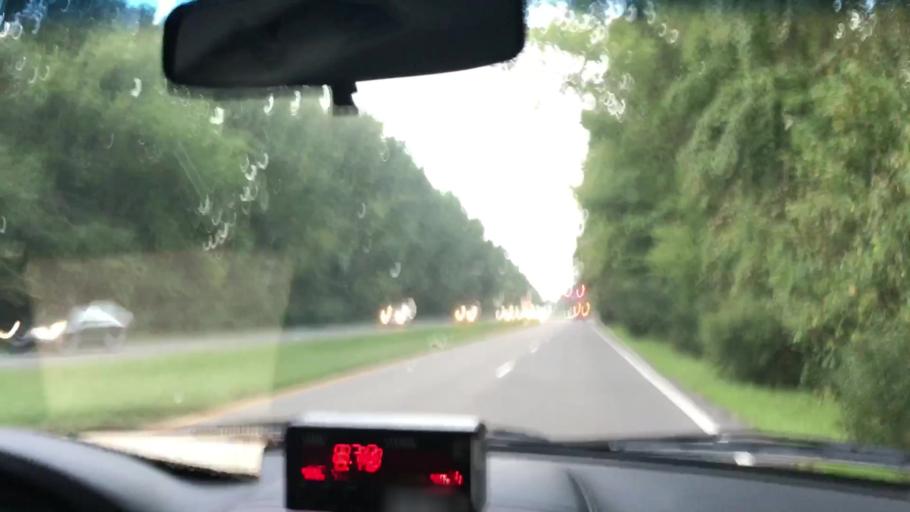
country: US
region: Virginia
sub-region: City of Hampton
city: Hampton
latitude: 37.0614
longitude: -76.3660
